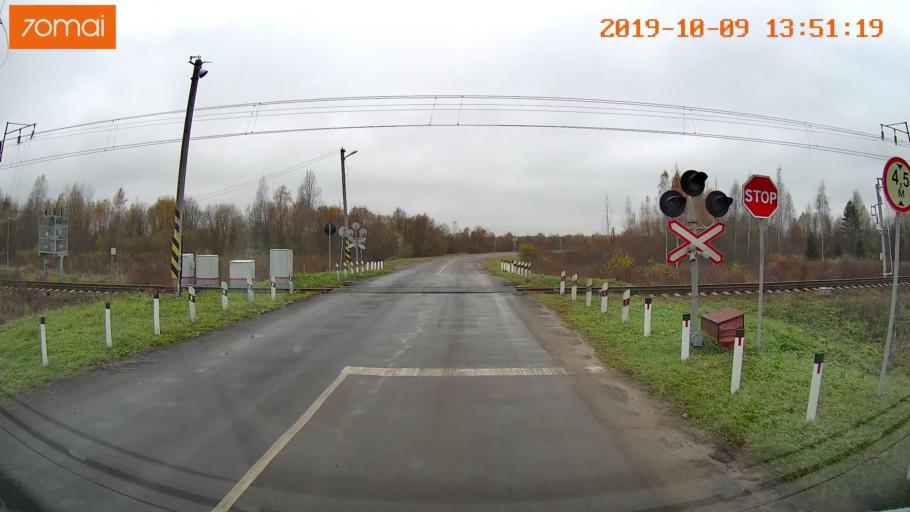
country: RU
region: Kostroma
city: Buy
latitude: 58.4073
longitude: 41.2411
